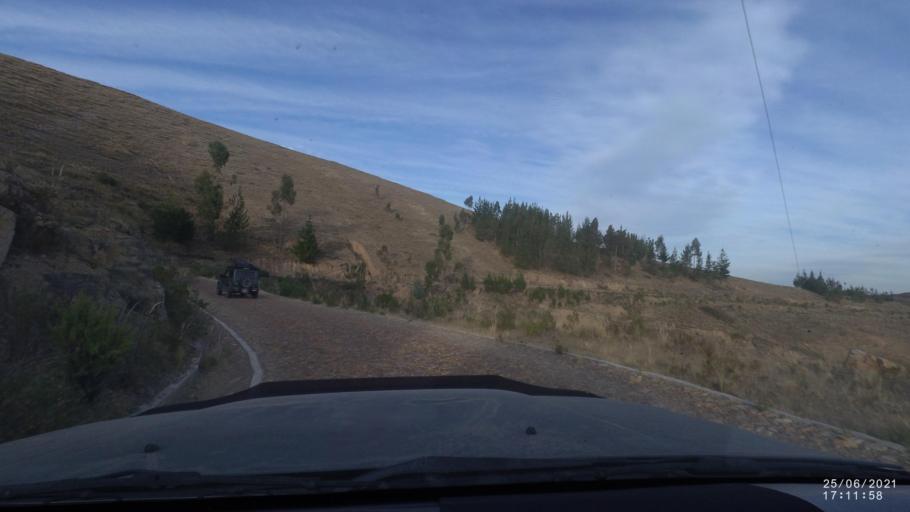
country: BO
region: Cochabamba
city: Arani
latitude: -17.8485
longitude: -65.7014
